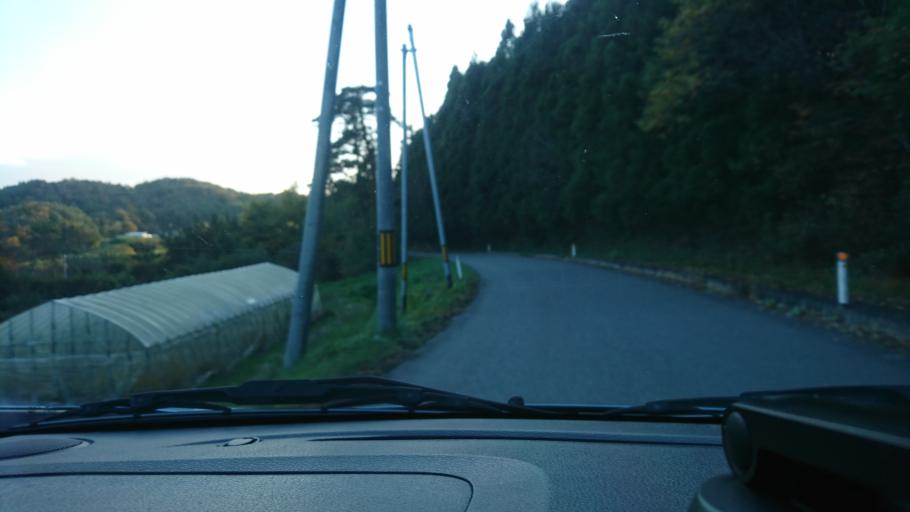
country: JP
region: Iwate
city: Ichinoseki
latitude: 38.7729
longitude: 141.2320
